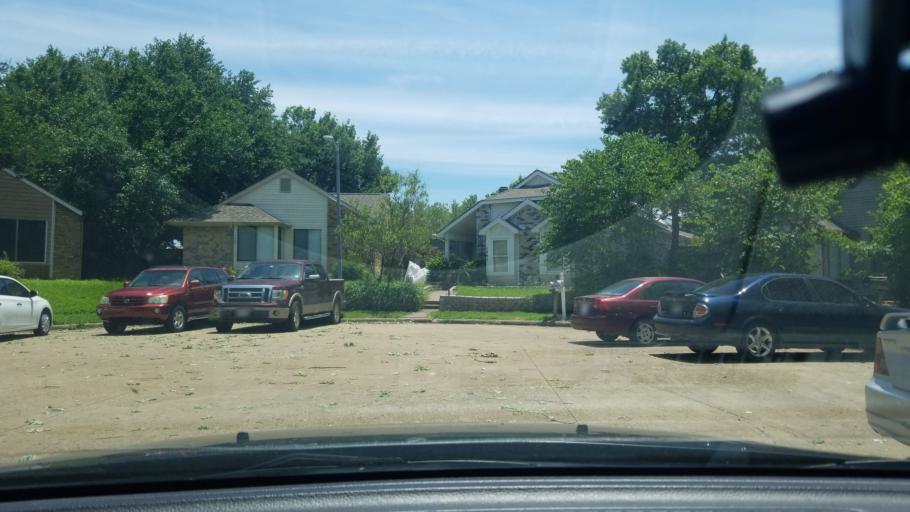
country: US
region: Texas
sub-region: Dallas County
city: Mesquite
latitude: 32.7831
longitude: -96.5988
